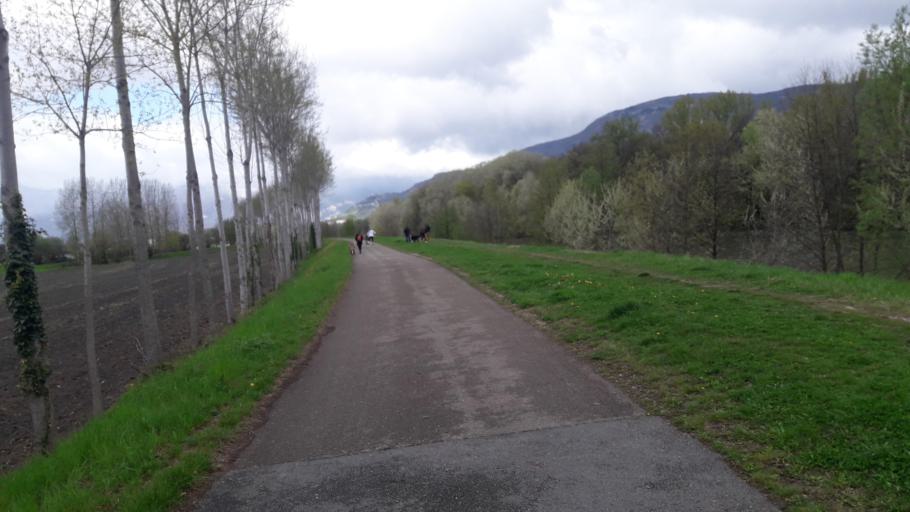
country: FR
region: Rhone-Alpes
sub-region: Departement de l'Isere
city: Gieres
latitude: 45.1888
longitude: 5.7964
